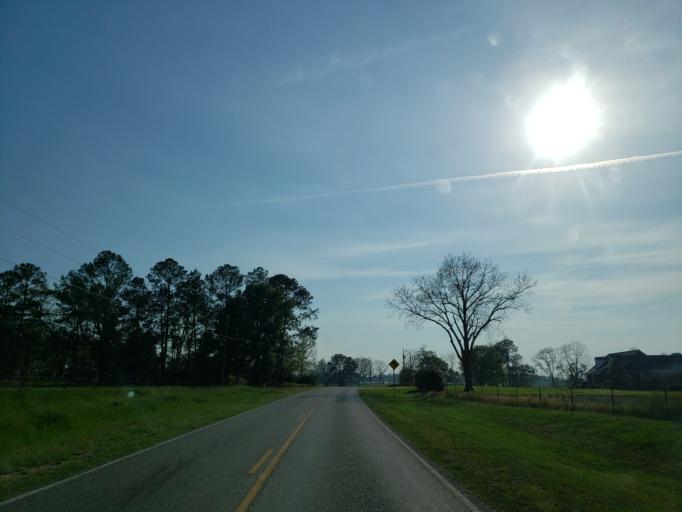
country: US
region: Georgia
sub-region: Tift County
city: Tifton
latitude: 31.5332
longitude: -83.5563
